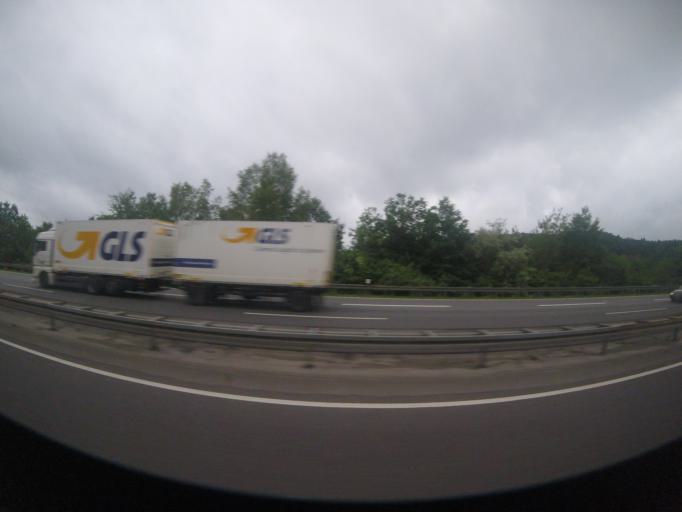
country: DE
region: Saarland
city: Friedrichsthal
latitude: 49.3259
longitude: 7.0748
